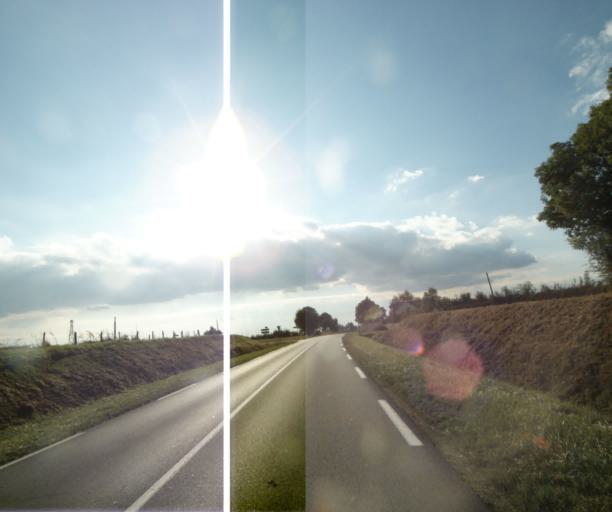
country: FR
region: Bourgogne
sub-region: Departement de Saone-et-Loire
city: Perrecy-les-Forges
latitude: 46.5987
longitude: 4.1438
